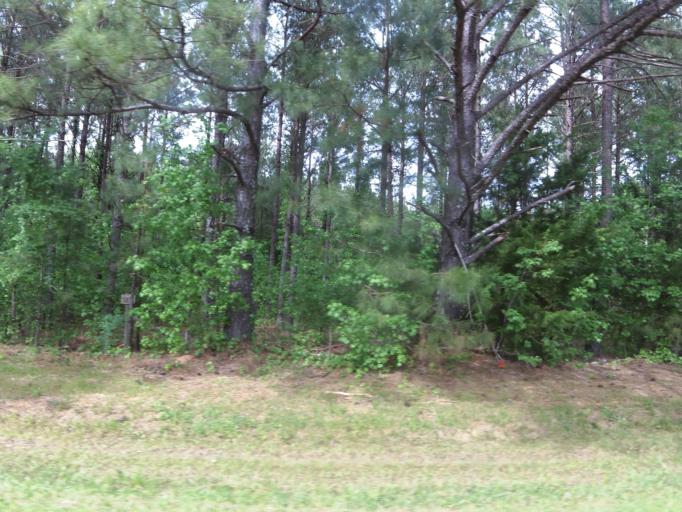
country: US
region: Georgia
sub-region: McDuffie County
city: Thomson
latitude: 33.5356
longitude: -82.4948
